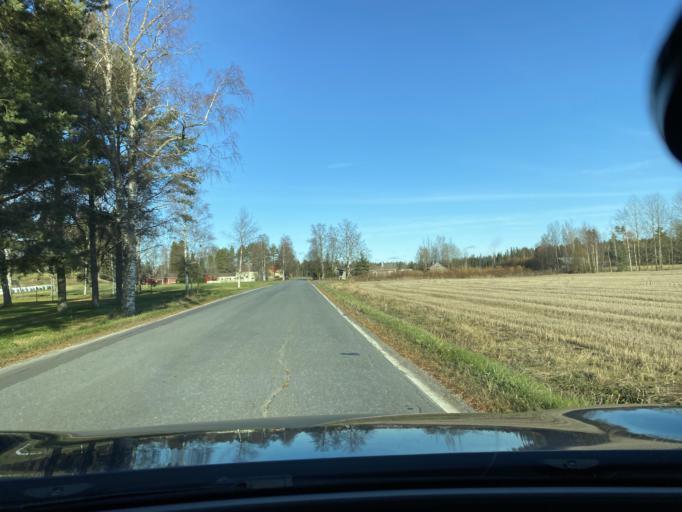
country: FI
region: Haeme
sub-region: Forssa
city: Tammela
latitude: 60.8715
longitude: 23.8457
